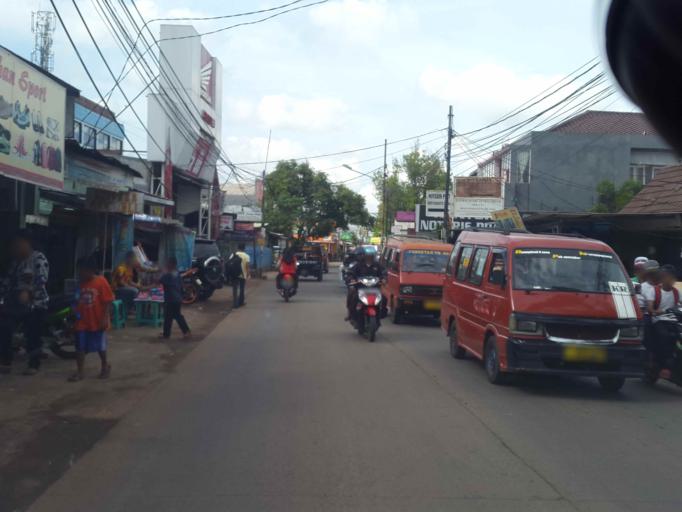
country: ID
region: West Java
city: Cileungsir
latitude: -6.3052
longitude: 106.9237
